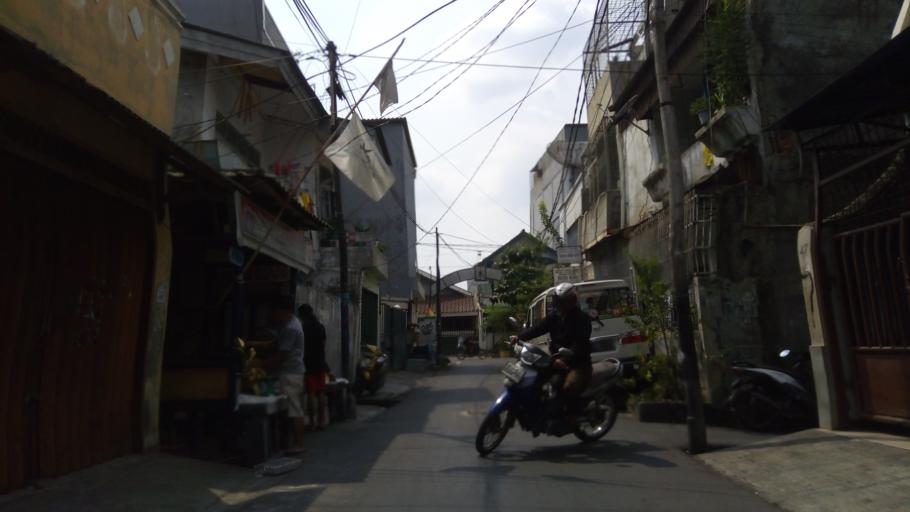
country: ID
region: Jakarta Raya
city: Jakarta
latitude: -6.1560
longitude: 106.8303
